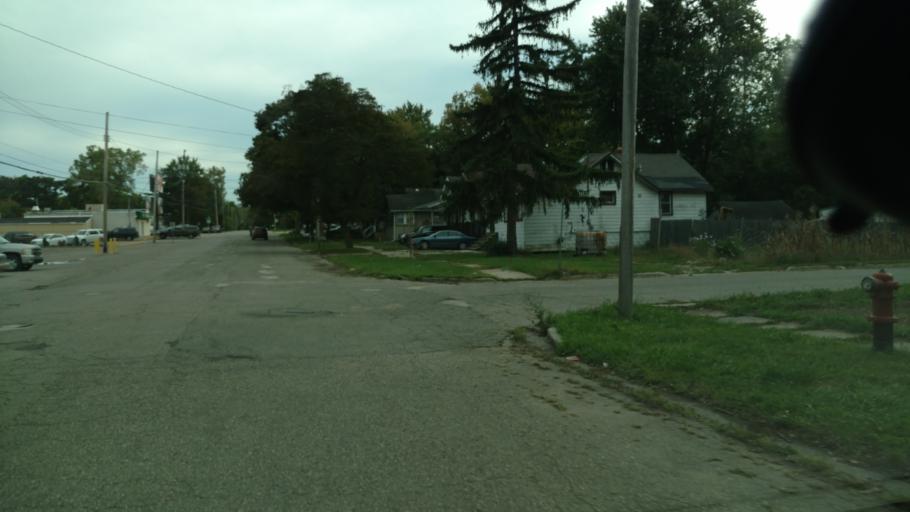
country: US
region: Michigan
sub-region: Ingham County
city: East Lansing
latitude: 42.7312
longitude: -84.5152
